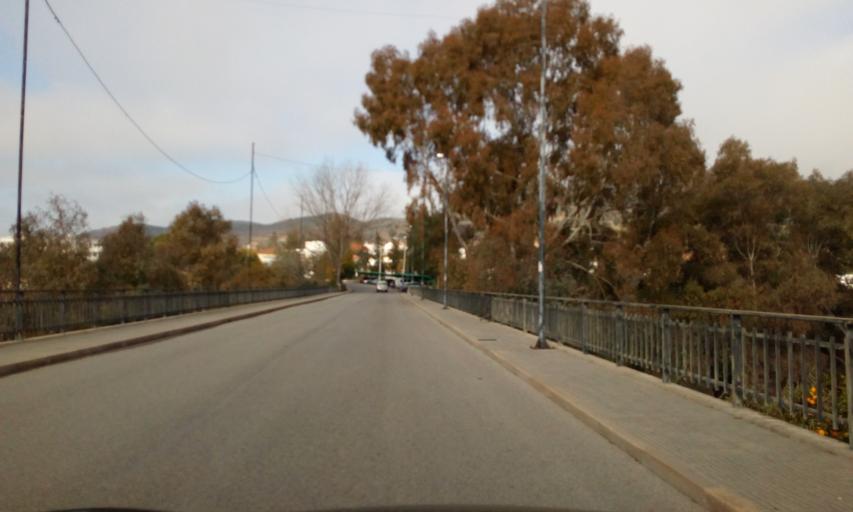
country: PT
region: Faro
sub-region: Alcoutim
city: Alcoutim
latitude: 37.4717
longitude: -7.4725
